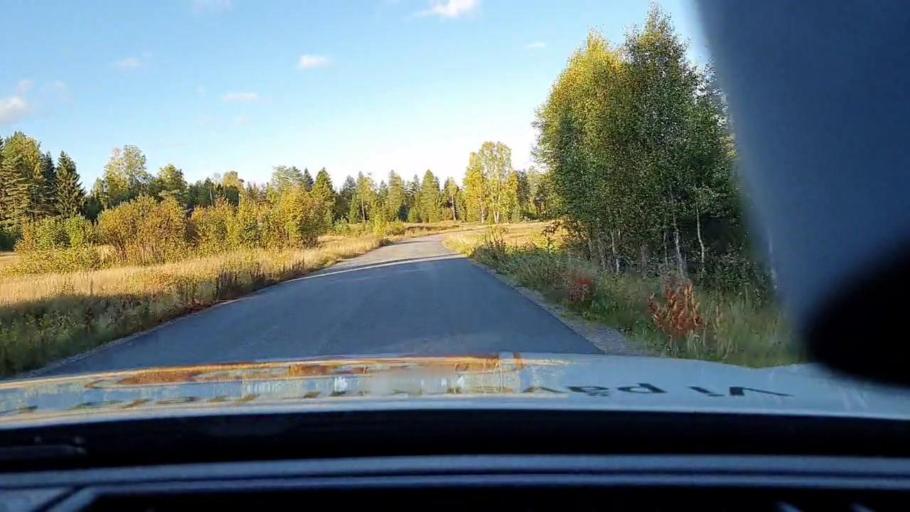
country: SE
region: Norrbotten
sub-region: Bodens Kommun
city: Saevast
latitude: 65.6478
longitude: 21.5553
